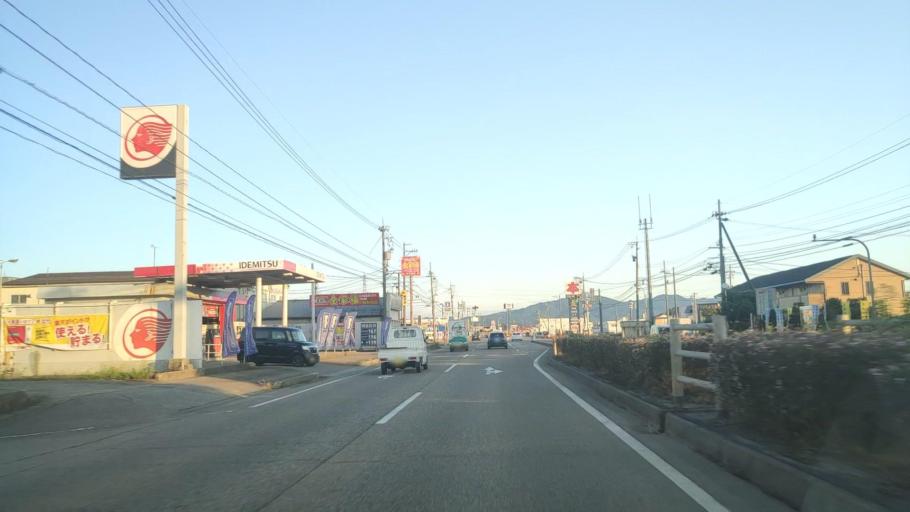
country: JP
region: Toyama
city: Himi
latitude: 36.8385
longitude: 136.9872
